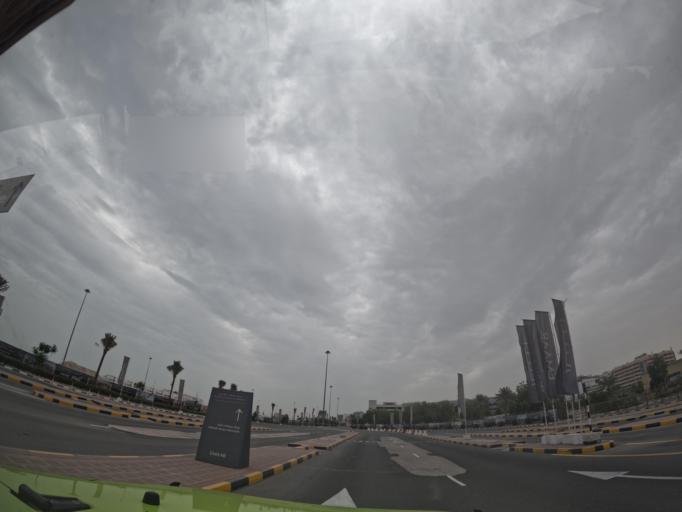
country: AE
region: Ash Shariqah
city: Sharjah
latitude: 25.2540
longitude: 55.2810
